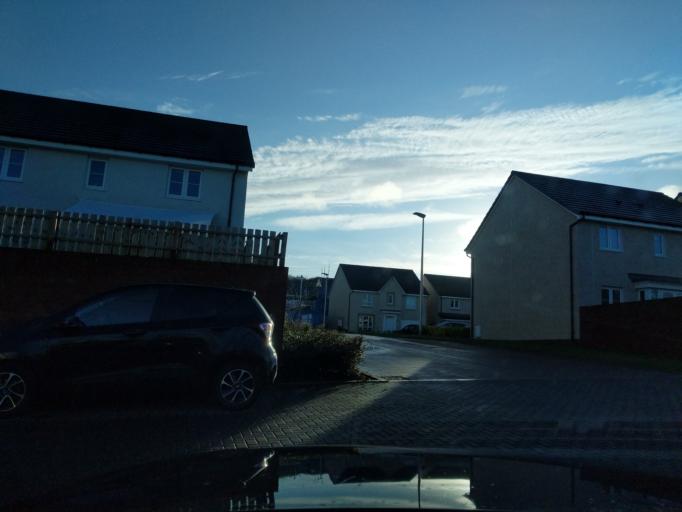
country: GB
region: Scotland
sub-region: Midlothian
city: Loanhead
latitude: 55.8945
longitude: -3.1571
